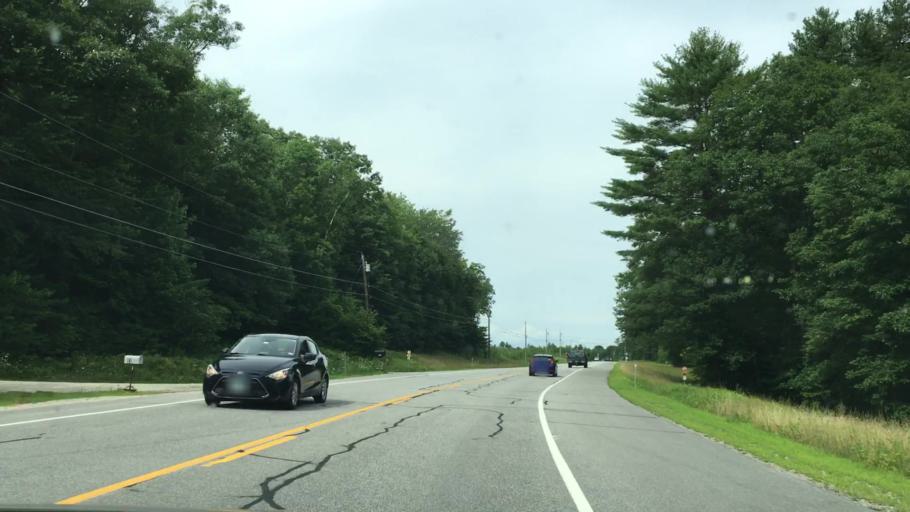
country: US
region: New Hampshire
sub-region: Hillsborough County
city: Hillsborough
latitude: 43.0966
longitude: -71.9200
